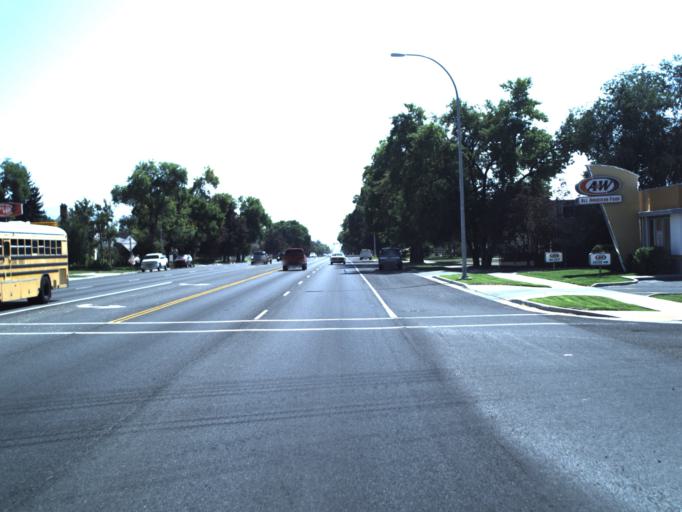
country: US
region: Utah
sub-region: Cache County
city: Smithfield
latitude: 41.8346
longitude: -111.8328
